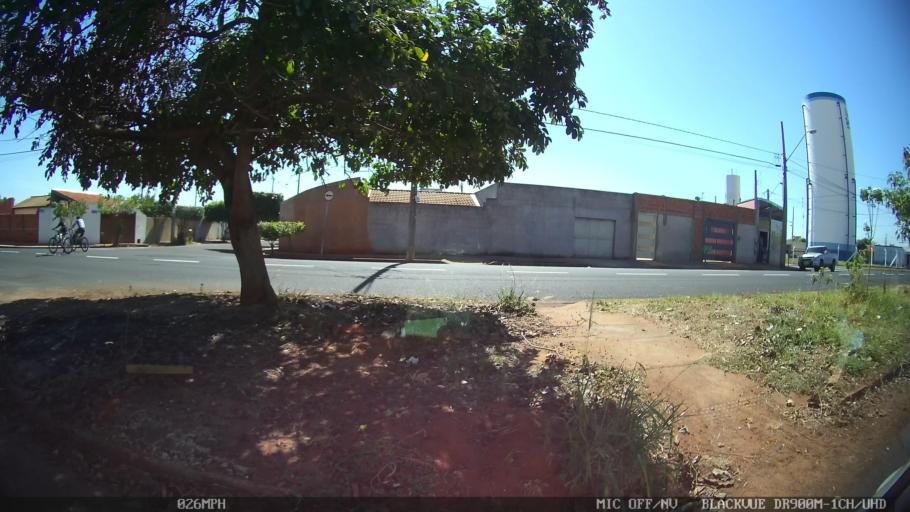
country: BR
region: Sao Paulo
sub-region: Sao Jose Do Rio Preto
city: Sao Jose do Rio Preto
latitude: -20.7405
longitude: -49.4167
